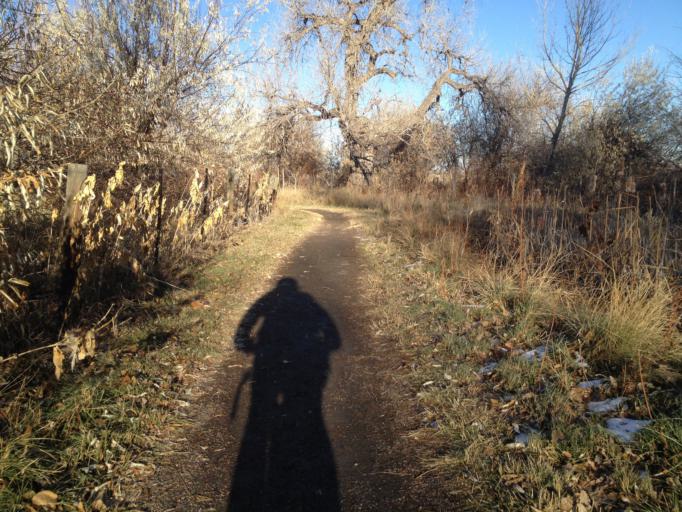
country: US
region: Colorado
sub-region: Boulder County
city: Gunbarrel
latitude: 40.0420
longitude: -105.1444
